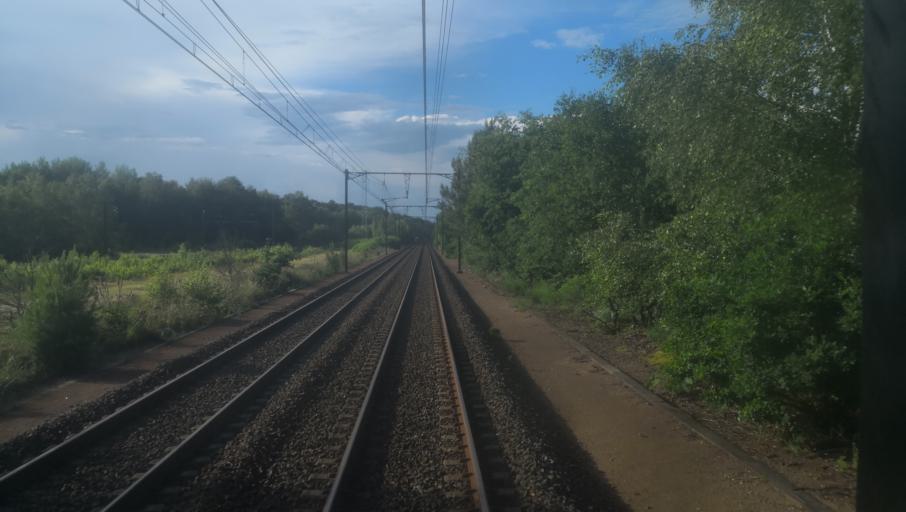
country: FR
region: Centre
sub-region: Departement du Loir-et-Cher
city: Salbris
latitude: 47.4429
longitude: 2.0437
